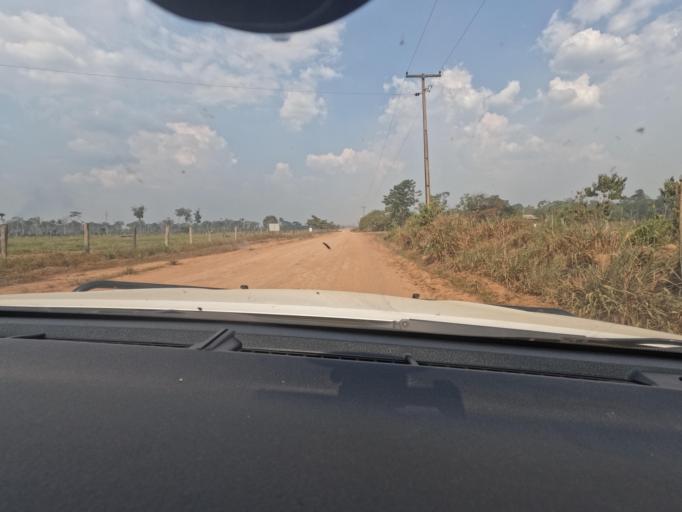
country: BR
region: Rondonia
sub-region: Porto Velho
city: Porto Velho
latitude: -8.6832
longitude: -63.2023
